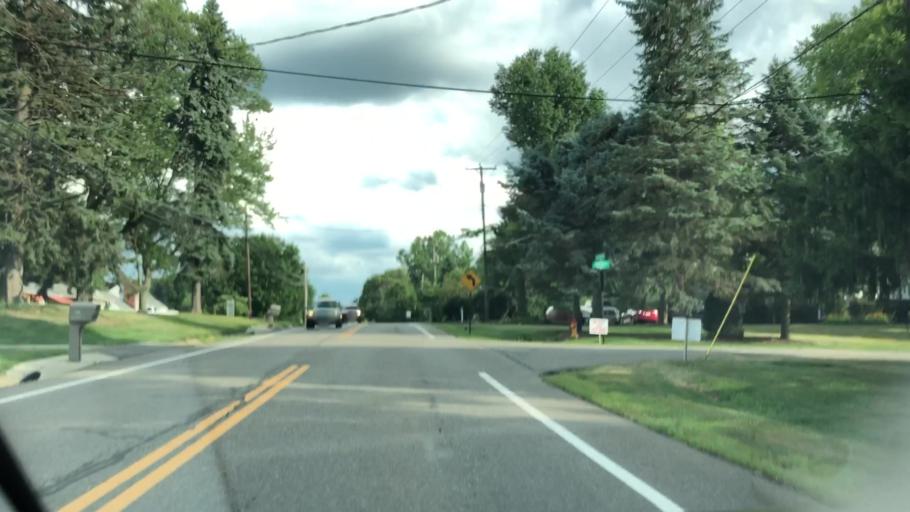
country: US
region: Ohio
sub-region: Summit County
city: Green
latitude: 40.9353
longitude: -81.4808
